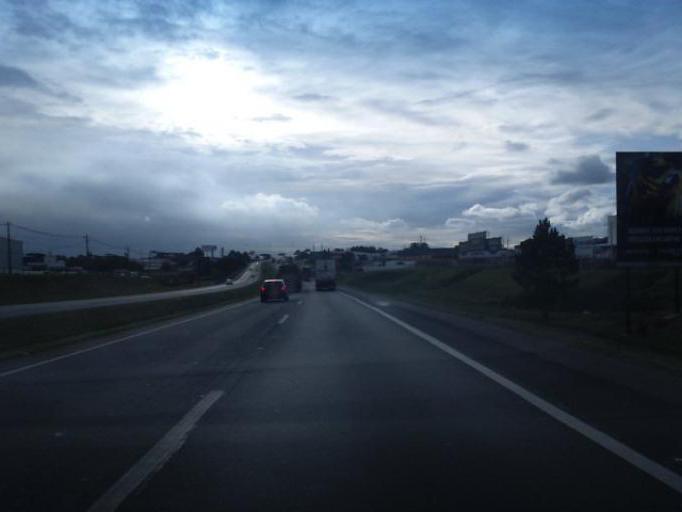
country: BR
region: Parana
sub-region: Sao Jose Dos Pinhais
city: Sao Jose dos Pinhais
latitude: -25.5659
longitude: -49.1660
